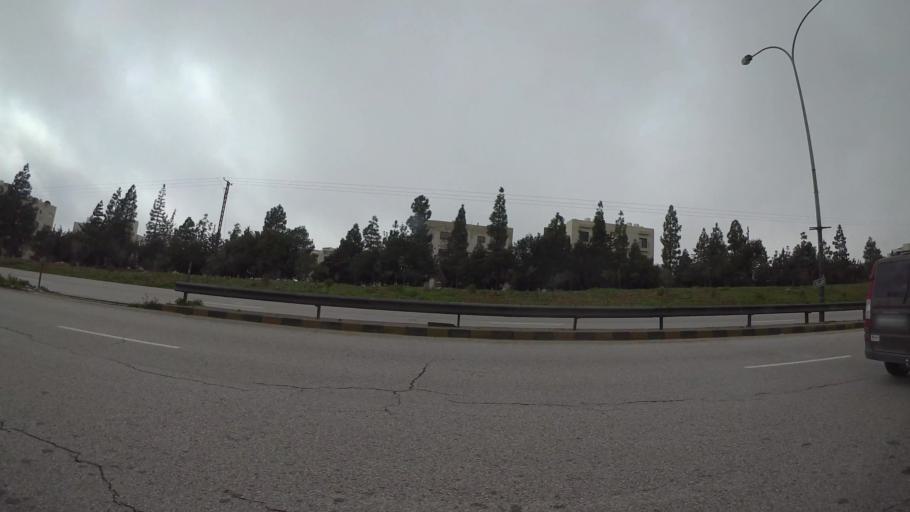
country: JO
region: Amman
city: Wadi as Sir
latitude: 31.9387
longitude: 35.8546
